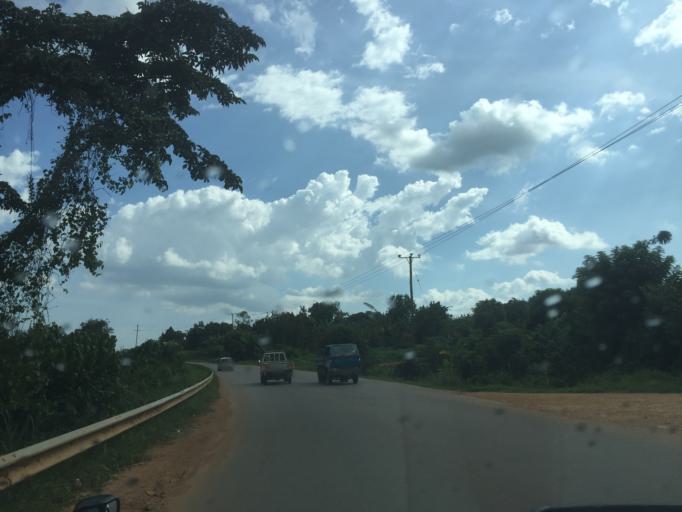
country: UG
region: Central Region
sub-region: Wakiso District
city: Wakiso
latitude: 0.5269
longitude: 32.5266
